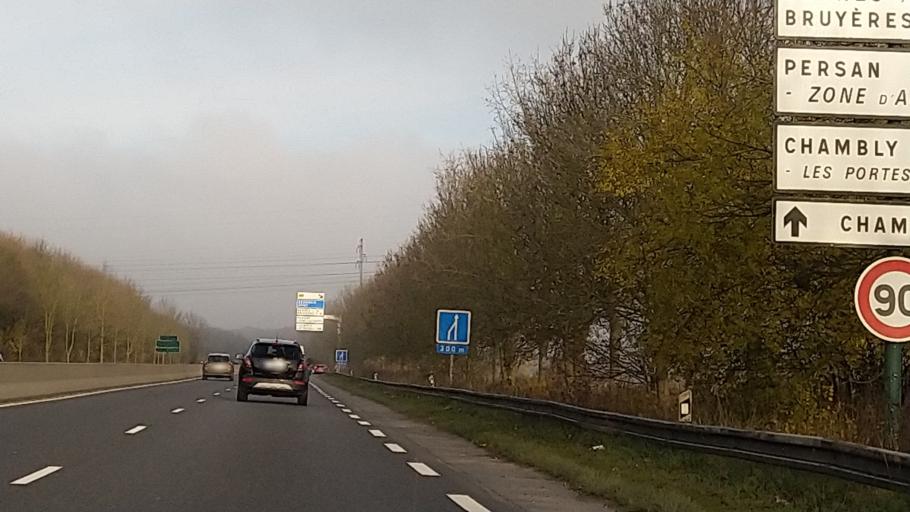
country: FR
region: Ile-de-France
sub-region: Departement du Val-d'Oise
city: Champagne-sur-Oise
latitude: 49.1455
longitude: 2.2501
